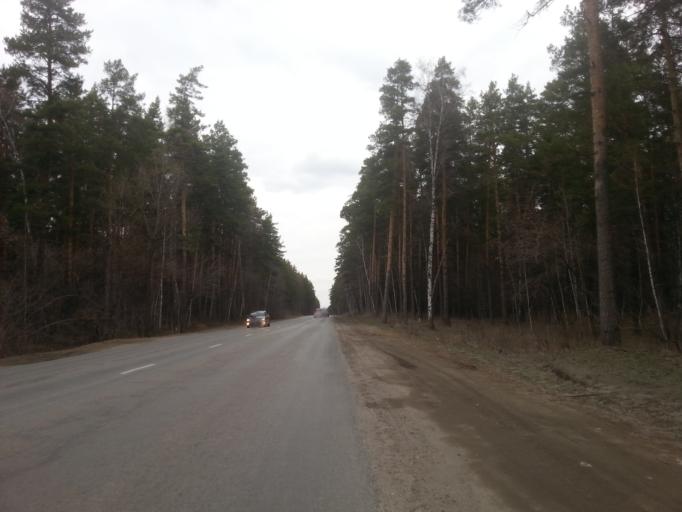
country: RU
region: Altai Krai
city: Yuzhnyy
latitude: 53.2793
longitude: 83.7179
